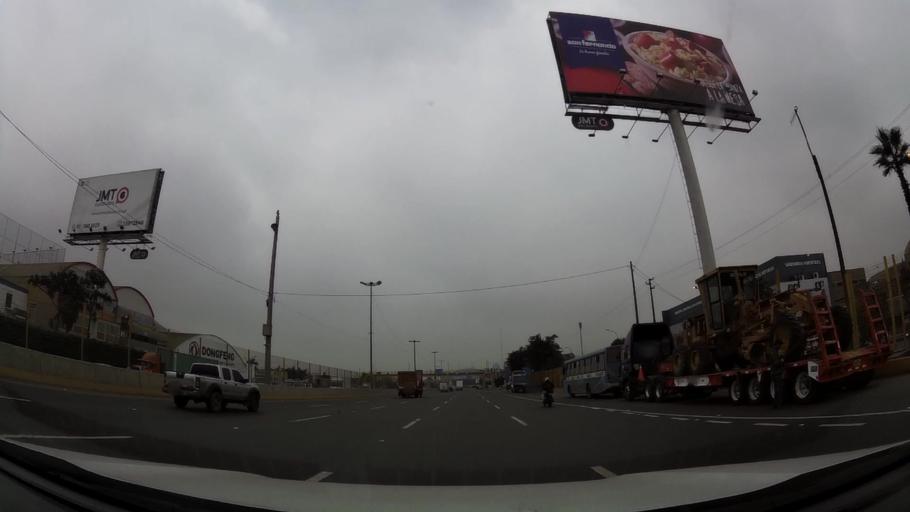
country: PE
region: Lima
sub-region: Lima
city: San Luis
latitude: -12.0549
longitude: -76.9748
